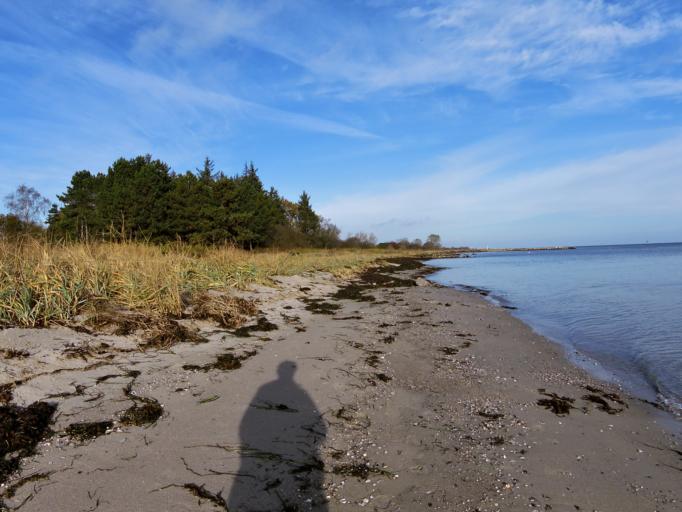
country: DK
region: Central Jutland
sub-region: Odder Kommune
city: Odder
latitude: 55.9226
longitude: 10.2567
